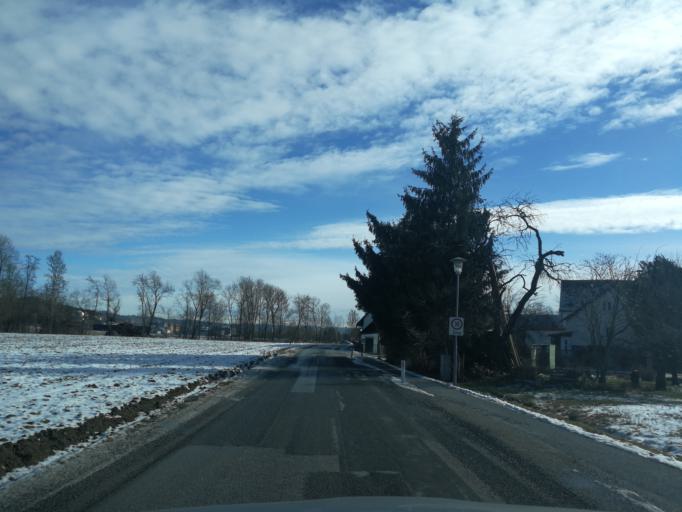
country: AT
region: Styria
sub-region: Politischer Bezirk Weiz
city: Ungerdorf
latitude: 47.1014
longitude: 15.6723
